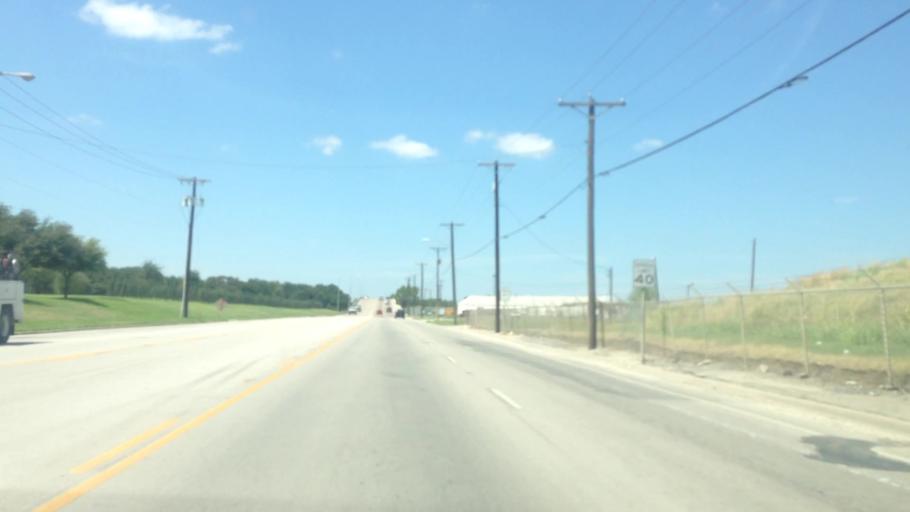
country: US
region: Texas
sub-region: Tarrant County
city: Haltom City
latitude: 32.7952
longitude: -97.3097
